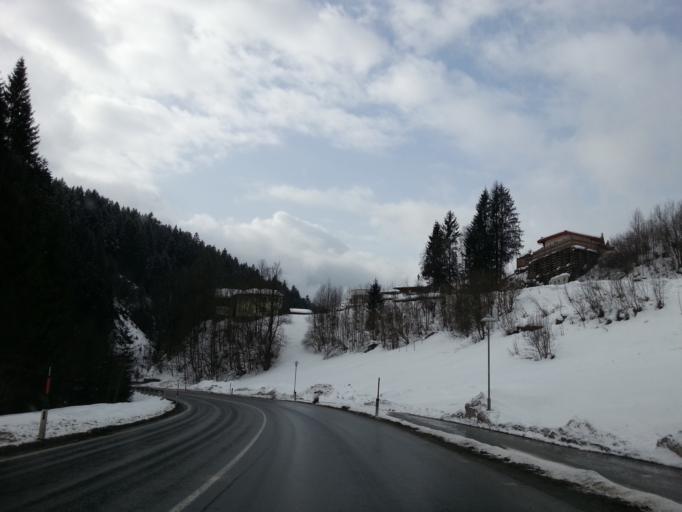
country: AT
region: Salzburg
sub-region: Politischer Bezirk Sankt Johann im Pongau
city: Eben im Pongau
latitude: 47.4352
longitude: 13.3567
